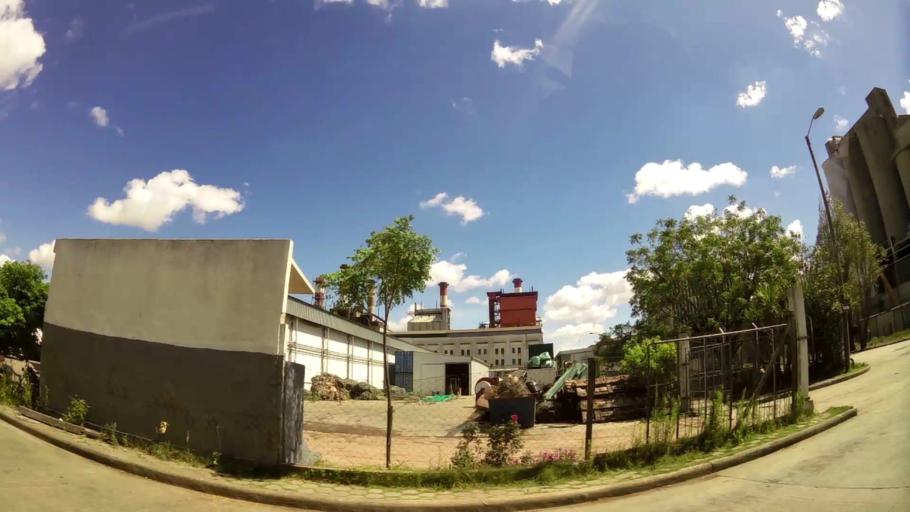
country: UY
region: Montevideo
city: Montevideo
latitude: -34.8879
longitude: -56.1960
